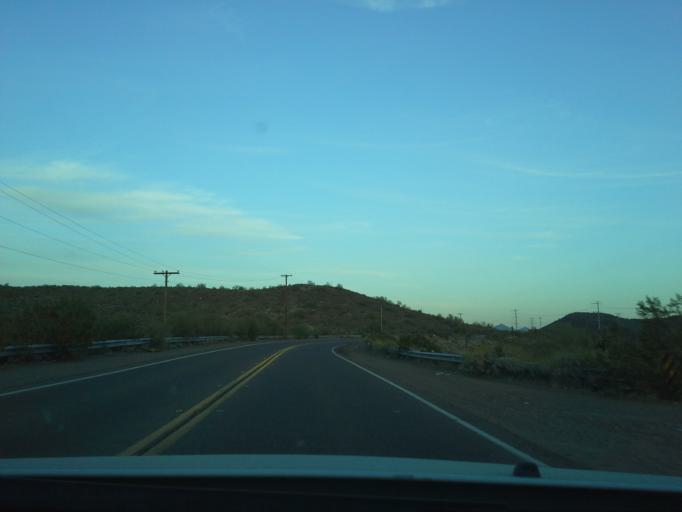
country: US
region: Arizona
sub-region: Maricopa County
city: Cave Creek
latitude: 33.7129
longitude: -112.0710
